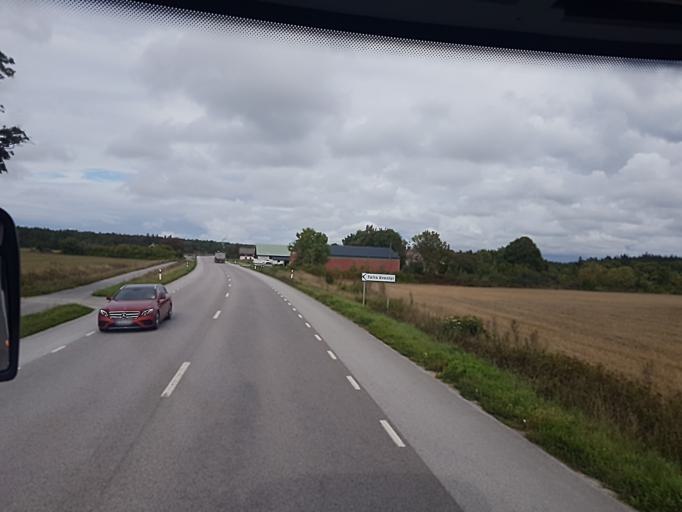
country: SE
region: Gotland
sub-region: Gotland
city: Vibble
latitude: 57.5289
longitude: 18.1761
